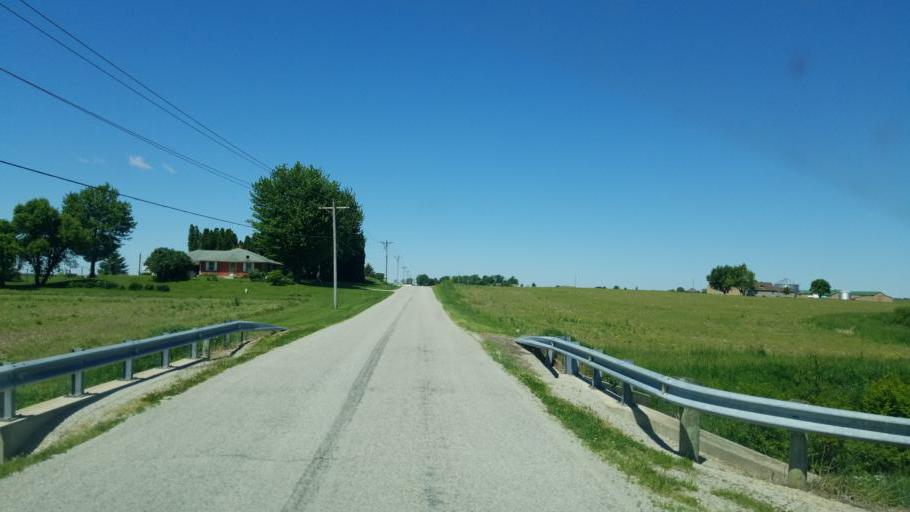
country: US
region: Ohio
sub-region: Shelby County
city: Anna
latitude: 40.3727
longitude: -84.2482
